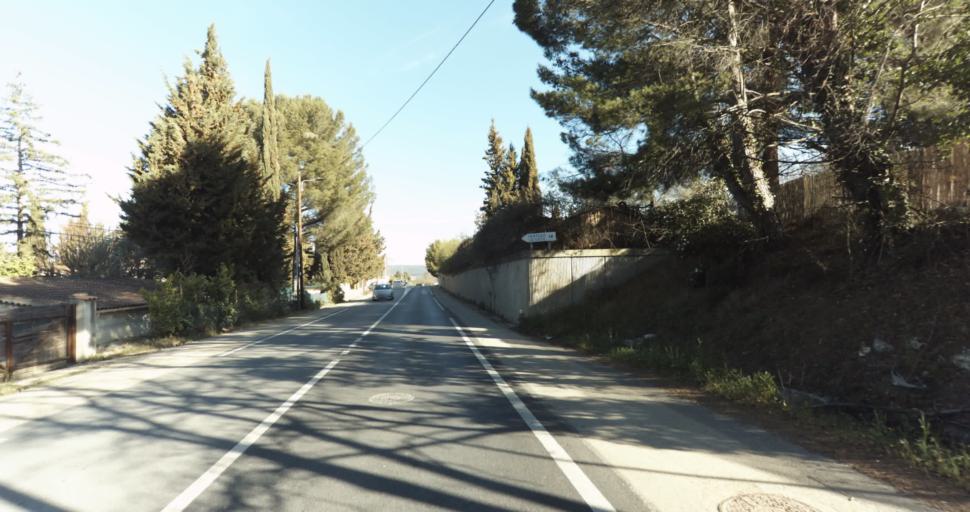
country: FR
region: Provence-Alpes-Cote d'Azur
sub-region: Departement des Bouches-du-Rhone
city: Aix-en-Provence
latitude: 43.5591
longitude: 5.4341
